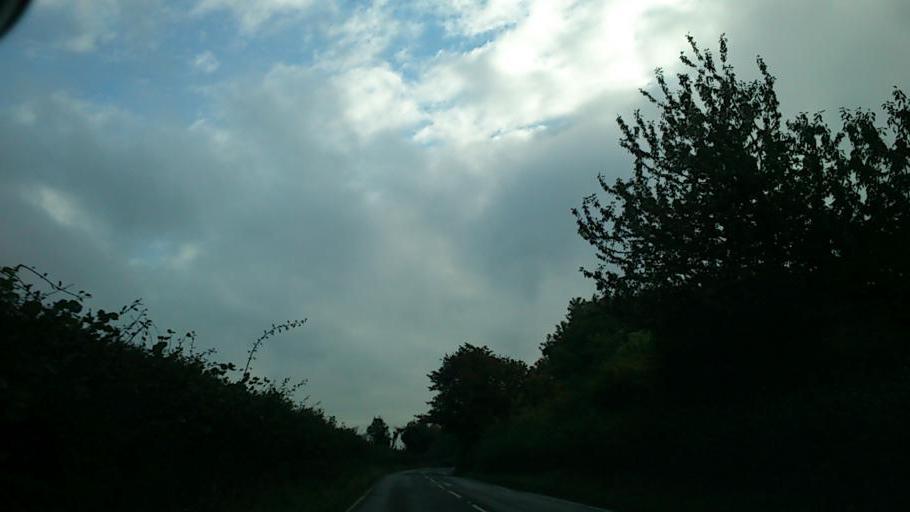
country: GB
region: Wales
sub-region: Sir Powys
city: Welshpool
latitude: 52.6500
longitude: -3.2132
